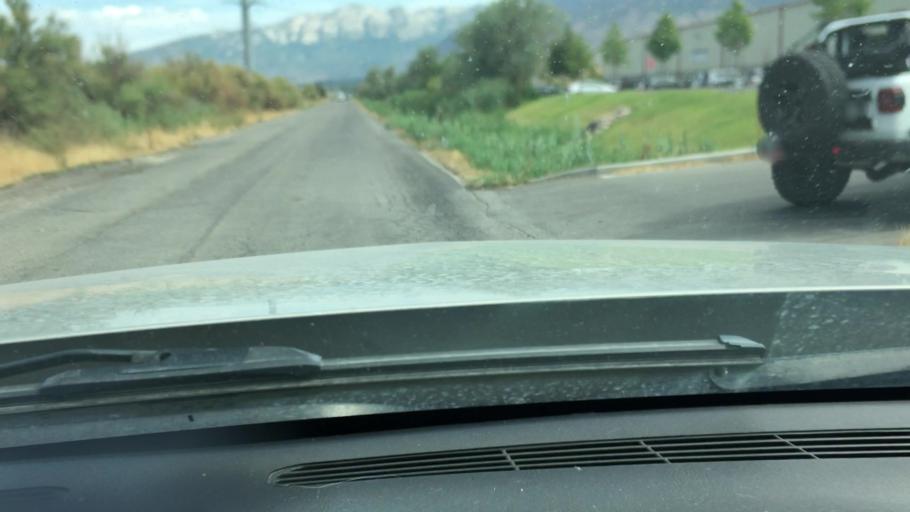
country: US
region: Utah
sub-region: Utah County
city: Pleasant Grove
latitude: 40.3354
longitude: -111.7599
